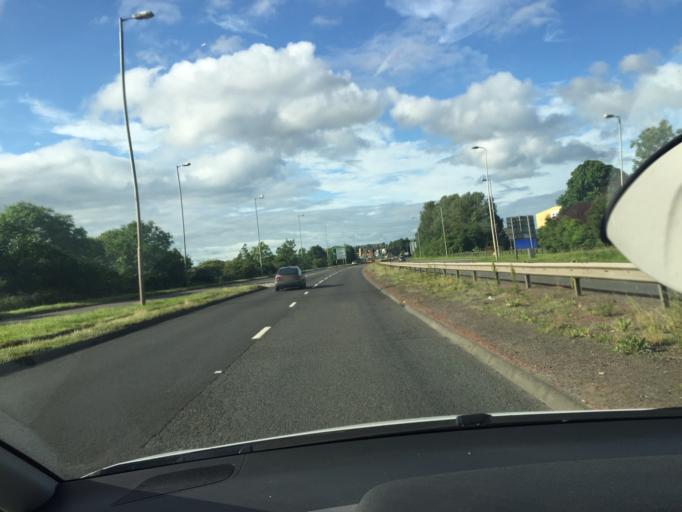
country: GB
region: Scotland
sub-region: North Lanarkshire
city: Bellshill
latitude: 55.8231
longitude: -4.0390
